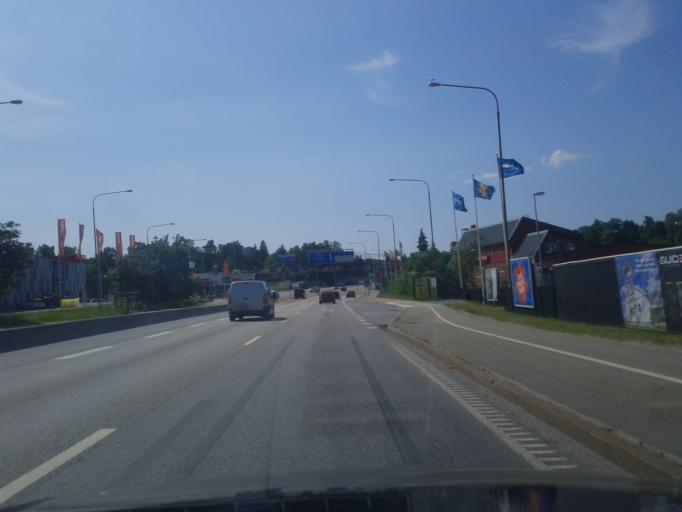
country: SE
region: Stockholm
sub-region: Huddinge Kommun
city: Huddinge
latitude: 59.2519
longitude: 18.0102
